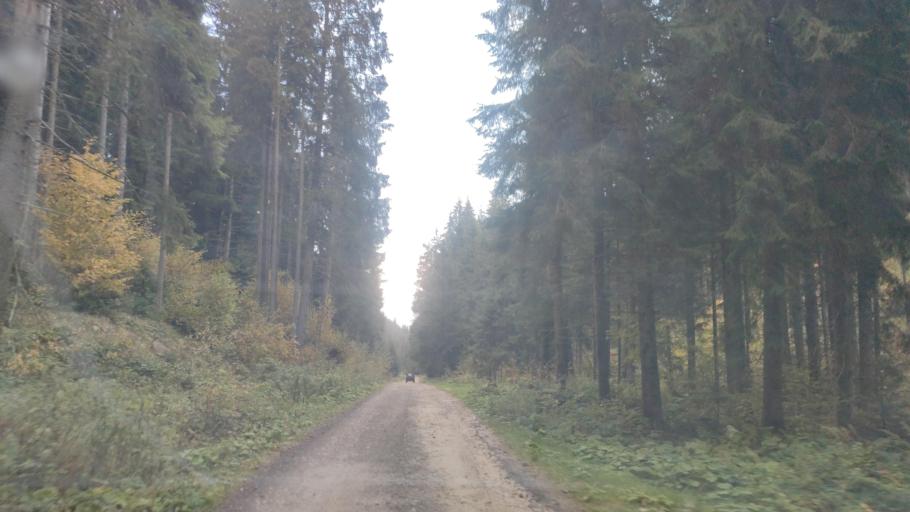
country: RO
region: Harghita
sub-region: Comuna Madaras
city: Madaras
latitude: 46.4783
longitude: 25.6522
